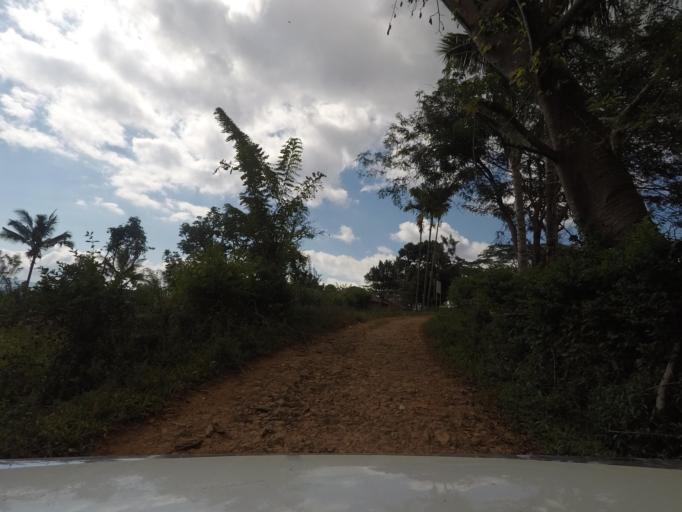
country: TL
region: Ermera
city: Gleno
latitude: -8.7194
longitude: 125.3209
